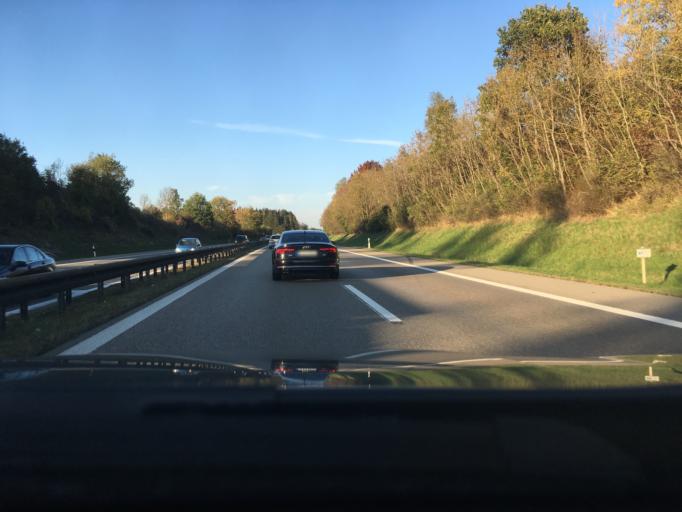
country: DE
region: Baden-Wuerttemberg
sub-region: Tuebingen Region
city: Aitrach
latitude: 47.9539
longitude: 10.1064
